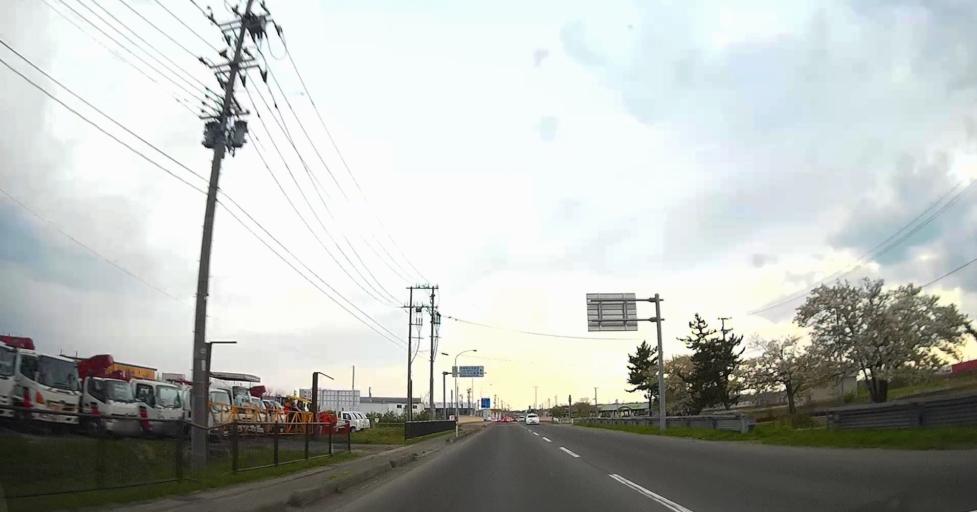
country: JP
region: Aomori
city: Aomori Shi
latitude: 40.8354
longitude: 140.6907
